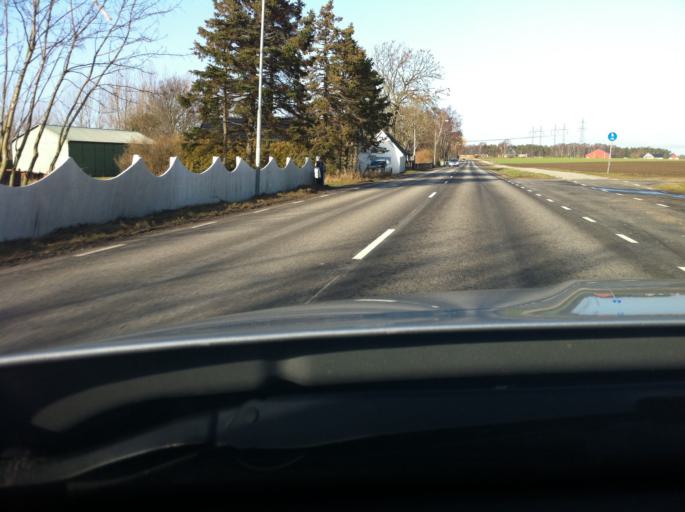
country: SE
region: Skane
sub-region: Kavlinge Kommun
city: Loddekopinge
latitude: 55.7822
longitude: 13.0065
